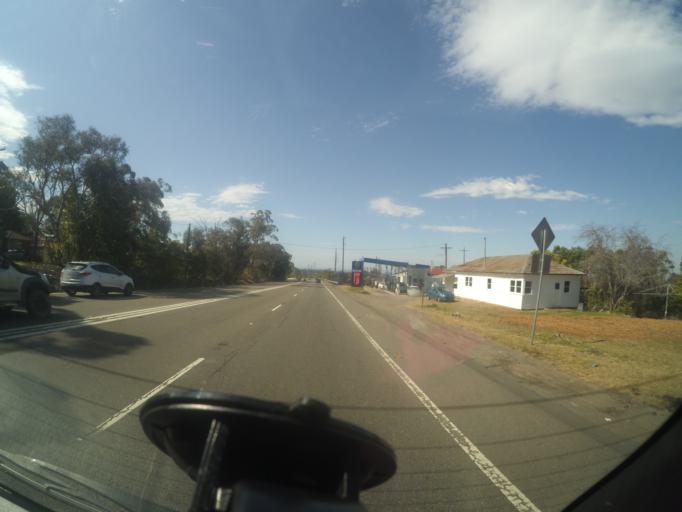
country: AU
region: New South Wales
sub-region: Blue Mountains Municipality
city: Hazelbrook
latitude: -33.7065
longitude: 150.5262
